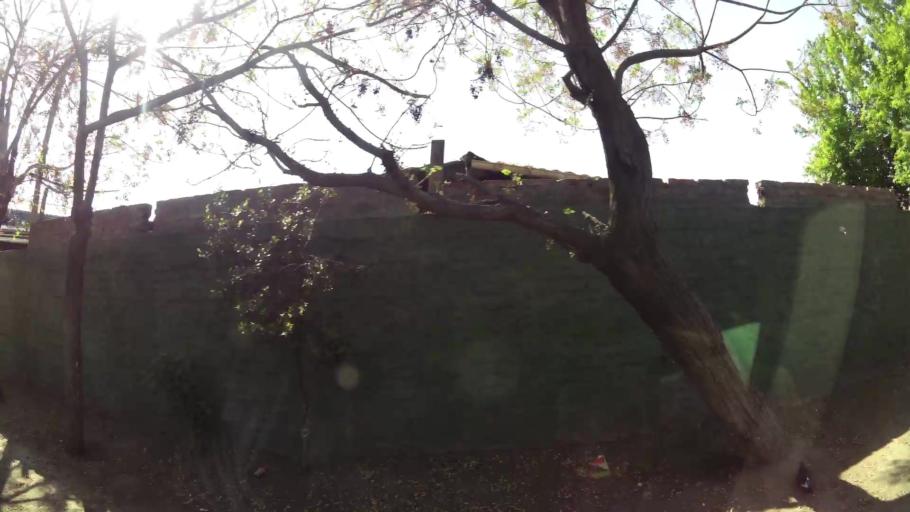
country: CL
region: Santiago Metropolitan
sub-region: Provincia de Santiago
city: La Pintana
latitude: -33.5335
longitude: -70.6040
